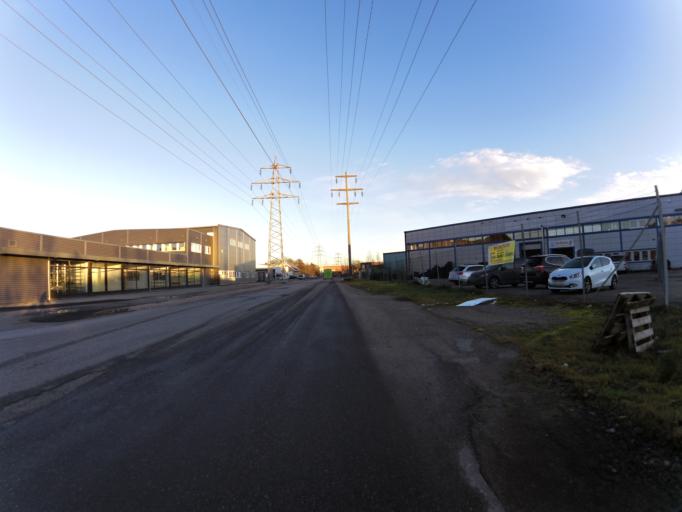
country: NO
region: Ostfold
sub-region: Fredrikstad
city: Fredrikstad
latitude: 59.2443
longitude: 10.9744
